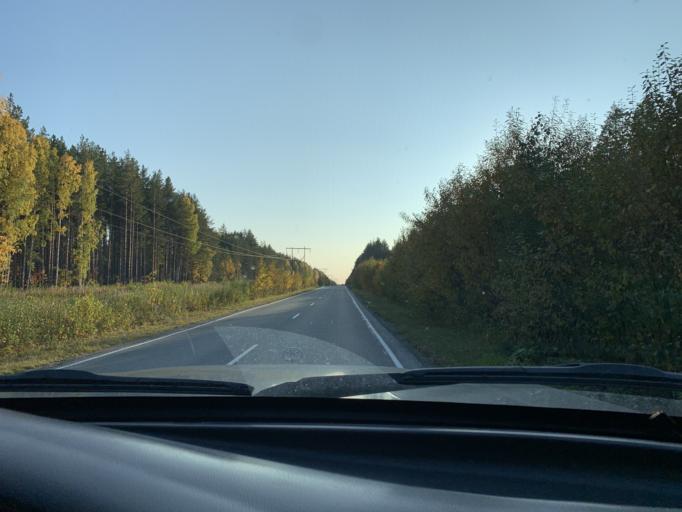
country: RU
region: Sverdlovsk
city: Verkhneye Dubrovo
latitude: 56.8733
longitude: 61.1068
